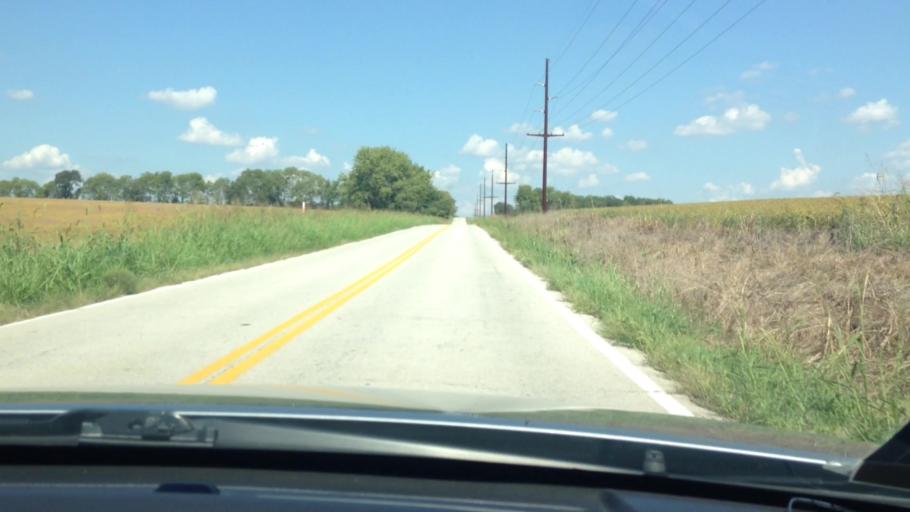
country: US
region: Missouri
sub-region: Platte County
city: Platte City
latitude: 39.3434
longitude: -94.7330
